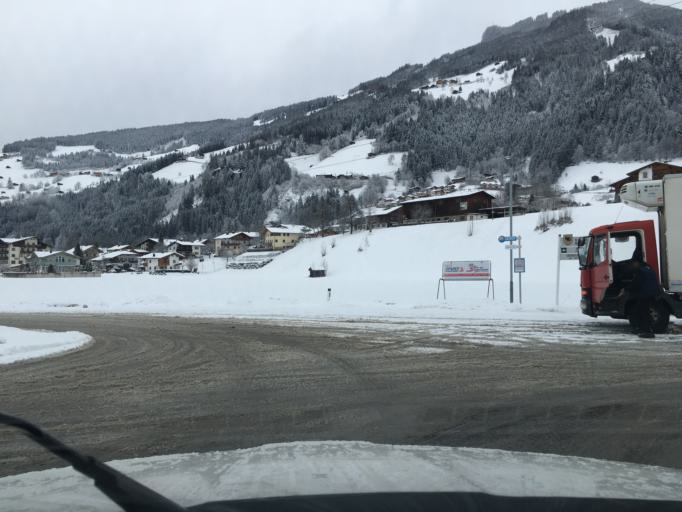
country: AT
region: Tyrol
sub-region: Politischer Bezirk Schwaz
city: Ramsau im Zillertal
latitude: 47.1935
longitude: 11.8709
